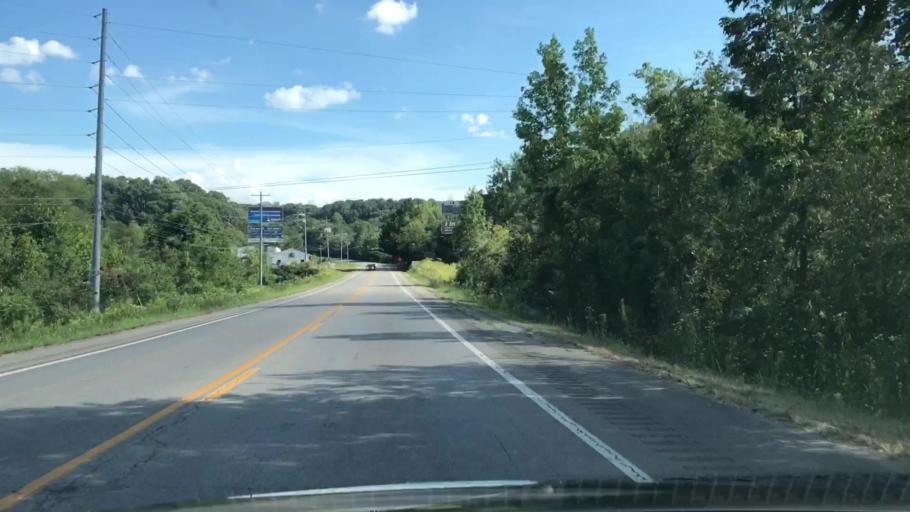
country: US
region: Alabama
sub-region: Limestone County
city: Ardmore
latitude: 35.0103
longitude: -86.8768
